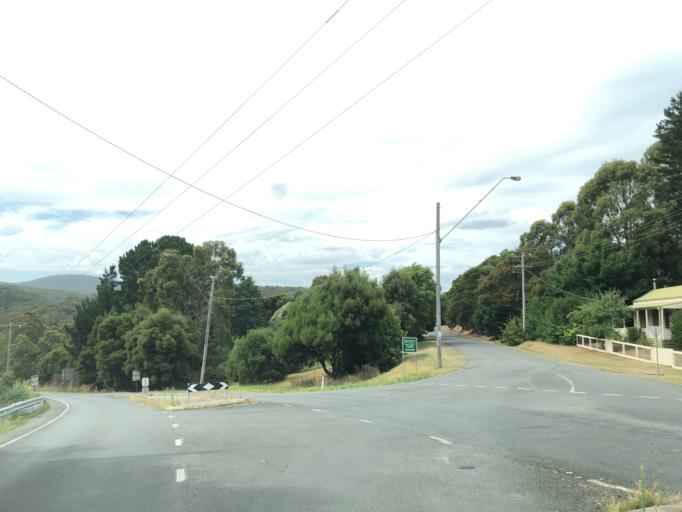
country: AU
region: Victoria
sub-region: Moorabool
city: Bacchus Marsh
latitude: -37.4723
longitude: 144.3063
